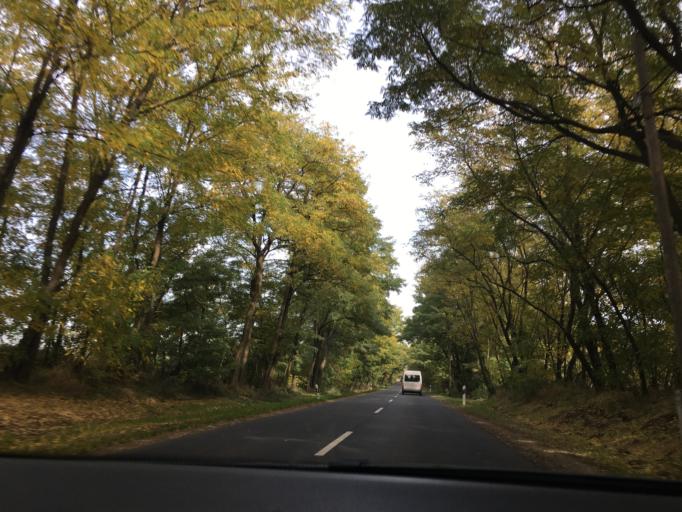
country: HU
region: Szabolcs-Szatmar-Bereg
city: Nagykallo
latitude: 47.8586
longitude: 21.8035
